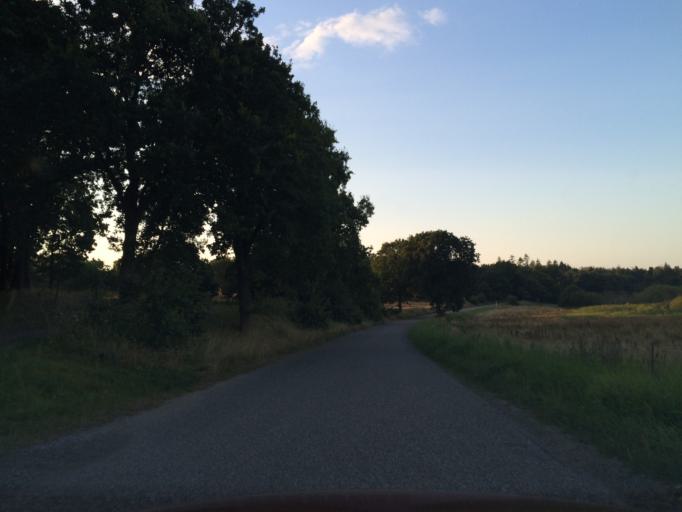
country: DK
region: Central Jutland
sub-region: Silkeborg Kommune
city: Svejbaek
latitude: 56.1998
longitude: 9.6462
